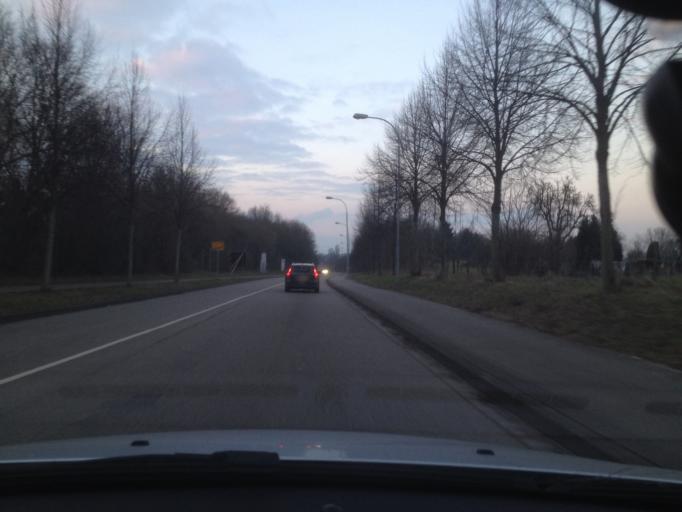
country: DE
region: Baden-Wuerttemberg
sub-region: Karlsruhe Region
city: Ettlingen
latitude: 48.9504
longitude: 8.4068
